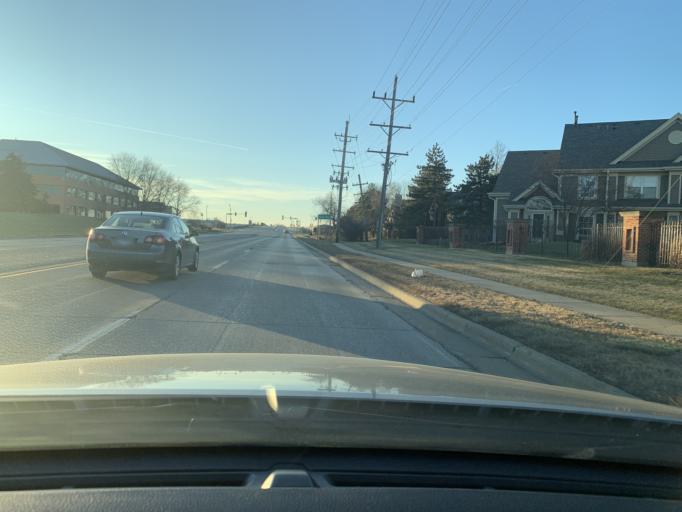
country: US
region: Illinois
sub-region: DuPage County
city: Itasca
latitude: 41.9925
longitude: -88.0177
